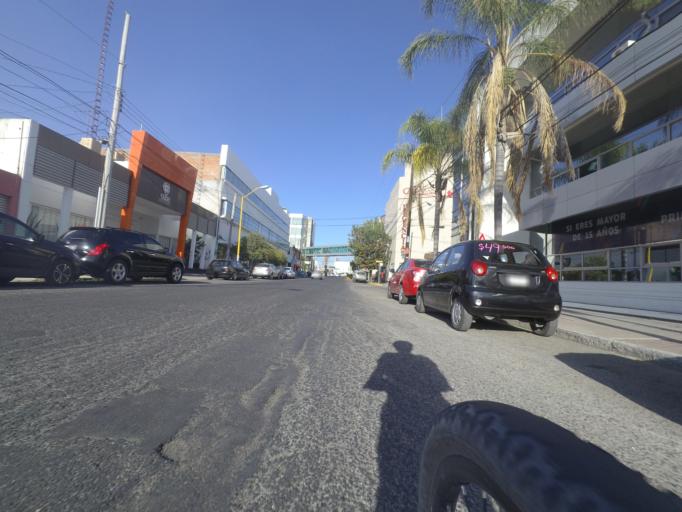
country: MX
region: Aguascalientes
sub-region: Aguascalientes
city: Aguascalientes
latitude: 21.8700
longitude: -102.2971
